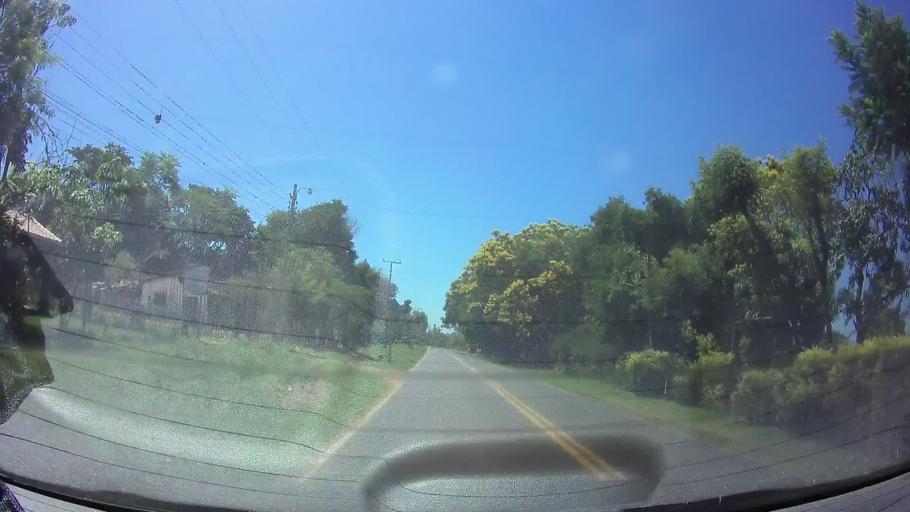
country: PY
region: Central
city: Aregua
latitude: -25.2773
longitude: -57.4052
